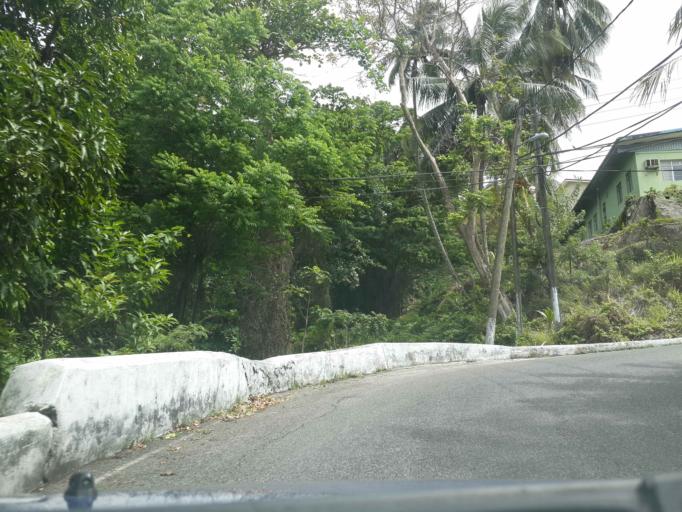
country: LC
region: Castries Quarter
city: Castries
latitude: 14.0066
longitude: -60.9925
